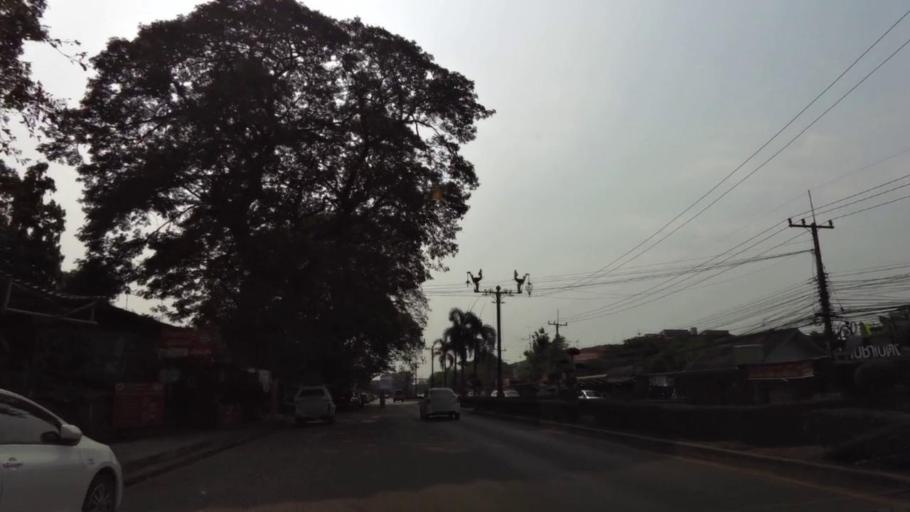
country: TH
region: Phra Nakhon Si Ayutthaya
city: Phra Nakhon Si Ayutthaya
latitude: 14.3463
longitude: 100.5625
